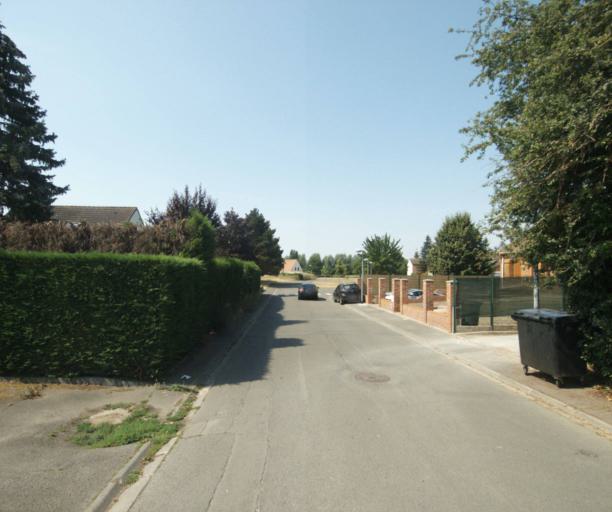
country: FR
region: Nord-Pas-de-Calais
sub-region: Departement du Nord
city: Comines
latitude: 50.7548
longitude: 3.0047
